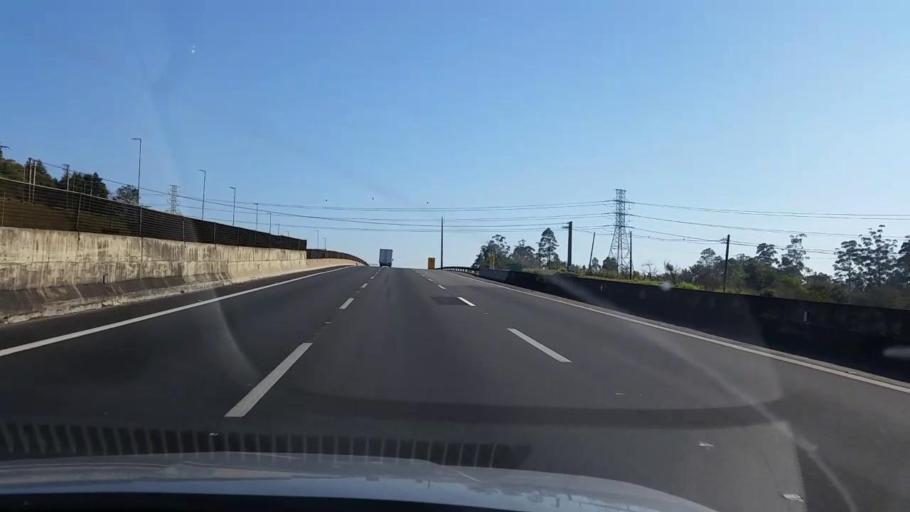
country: BR
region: Sao Paulo
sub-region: Varzea Paulista
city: Varzea Paulista
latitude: -23.2360
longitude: -46.8703
